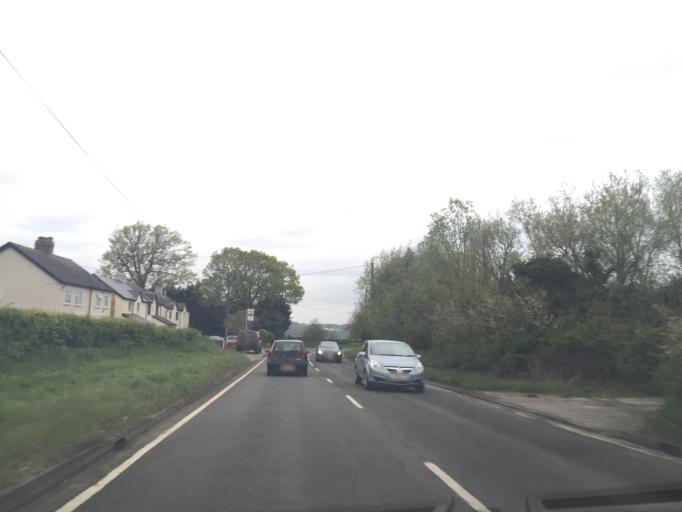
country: GB
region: England
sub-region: Greater London
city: Collier Row
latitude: 51.6445
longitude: 0.1653
